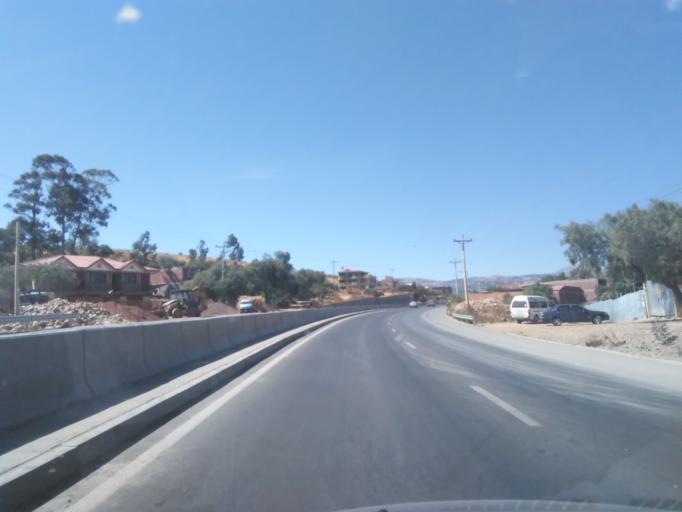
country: BO
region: Cochabamba
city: Colomi
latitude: -17.4059
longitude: -66.0061
